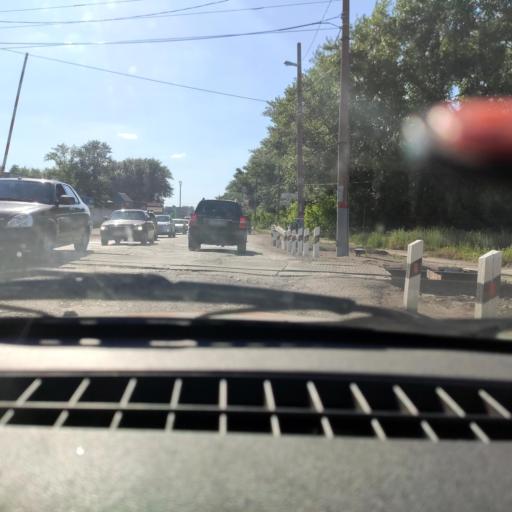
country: RU
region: Bashkortostan
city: Sterlitamak
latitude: 53.6534
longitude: 55.9662
